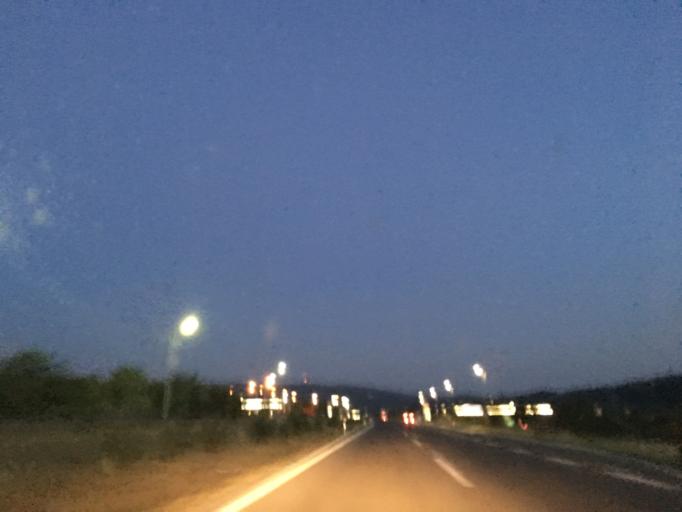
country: MK
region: Petrovec
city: Petrovec
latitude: 41.9065
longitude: 21.6521
